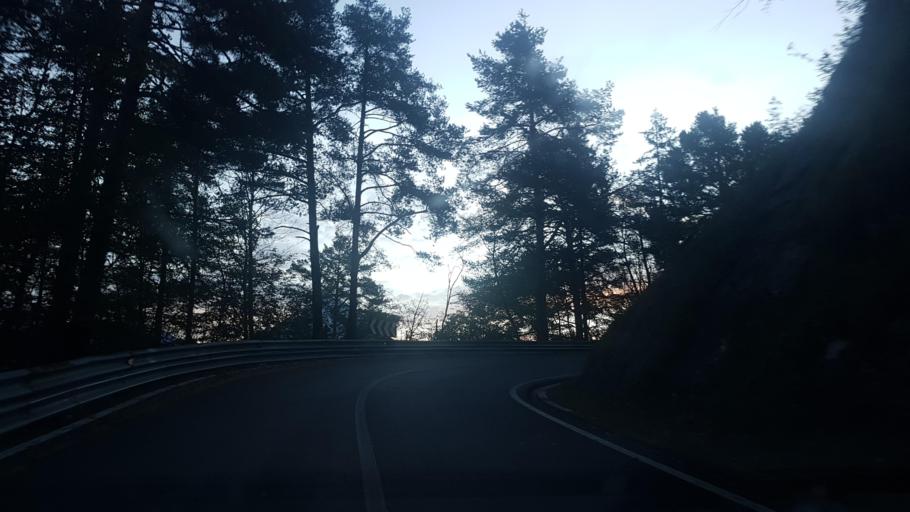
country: IT
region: Friuli Venezia Giulia
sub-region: Provincia di Udine
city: Chiaulis
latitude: 46.3758
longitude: 12.9615
